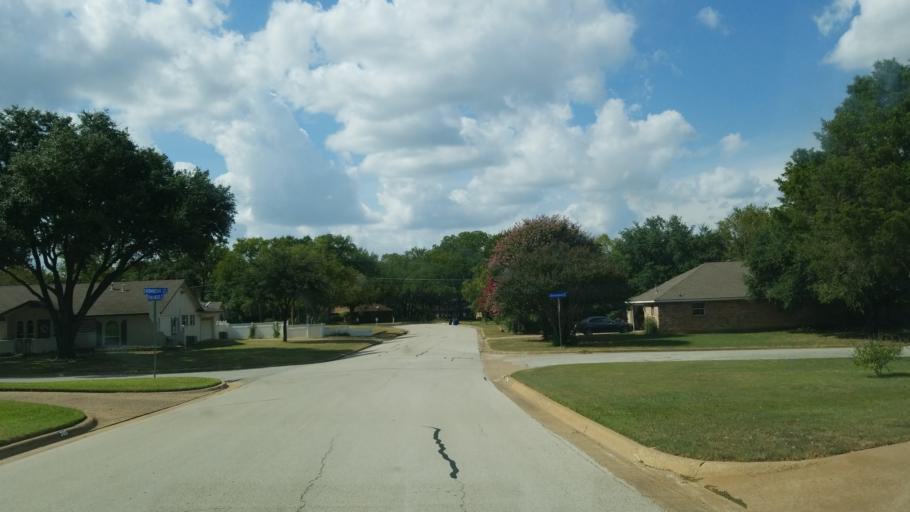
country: US
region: Texas
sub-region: Tarrant County
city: Euless
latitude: 32.8653
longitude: -97.0870
